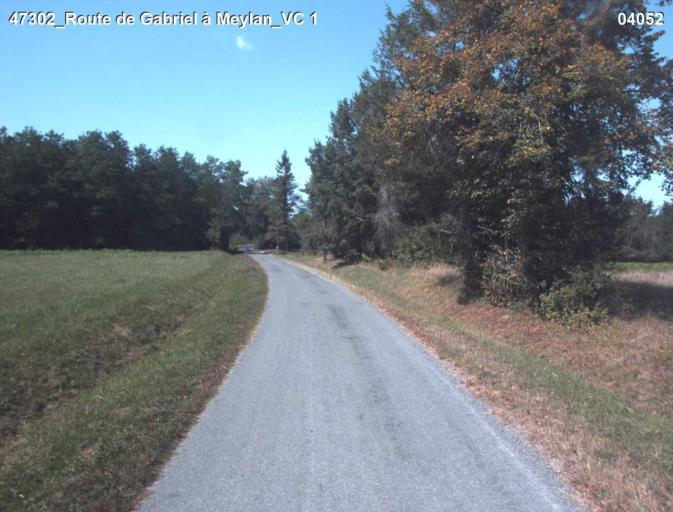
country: FR
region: Aquitaine
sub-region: Departement des Landes
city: Gabarret
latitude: 44.0773
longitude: 0.1165
